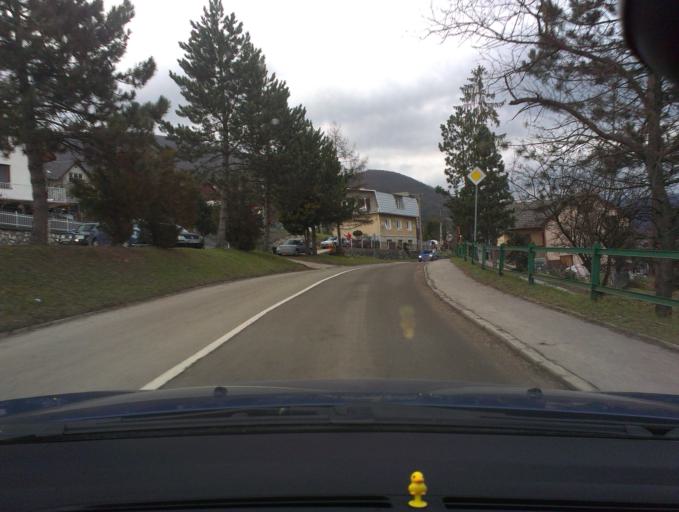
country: SK
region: Nitriansky
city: Trencianske Teplice
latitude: 48.9032
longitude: 18.2312
